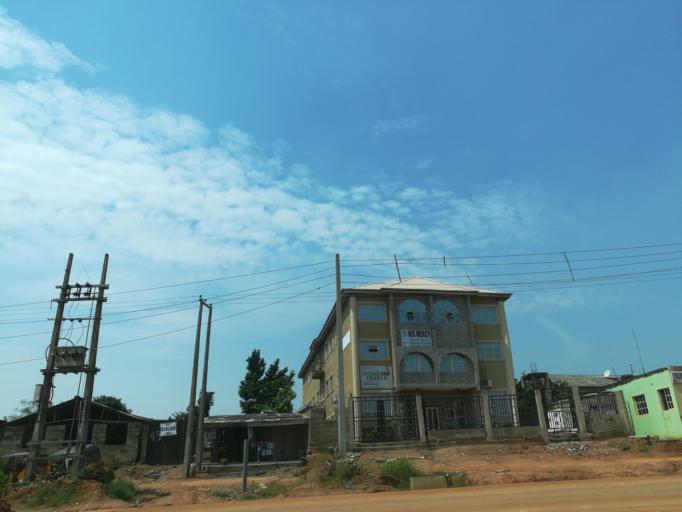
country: NG
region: Lagos
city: Ikorodu
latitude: 6.6588
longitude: 3.4736
